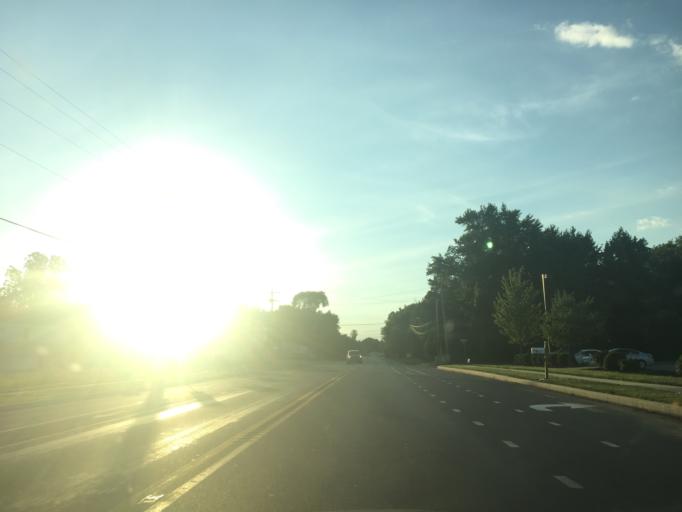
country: US
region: Delaware
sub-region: New Castle County
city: Townsend
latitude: 39.3980
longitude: -75.6845
